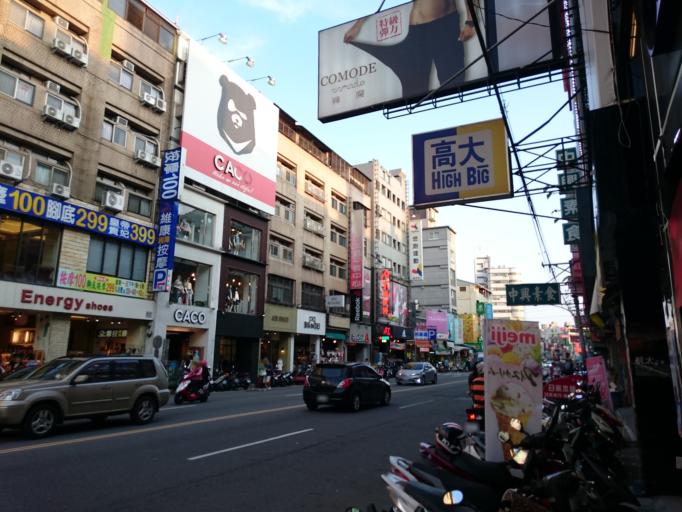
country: TW
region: Taiwan
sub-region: Taichung City
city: Taichung
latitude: 24.1786
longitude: 120.6452
